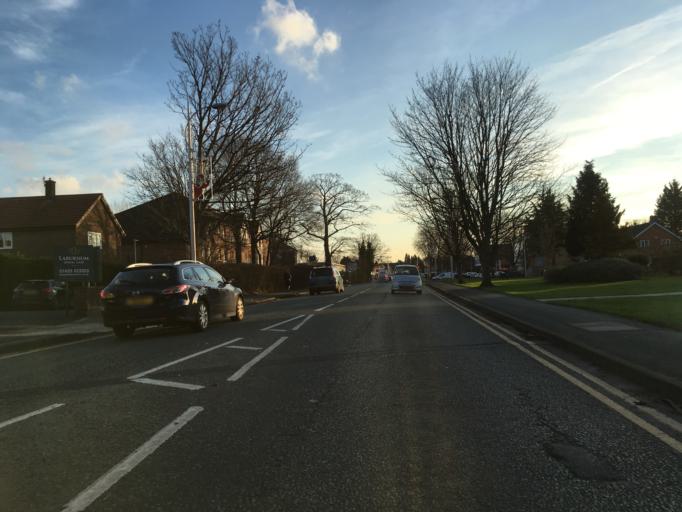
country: GB
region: England
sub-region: Cheshire East
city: Wilmslow
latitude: 53.3517
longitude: -2.2157
